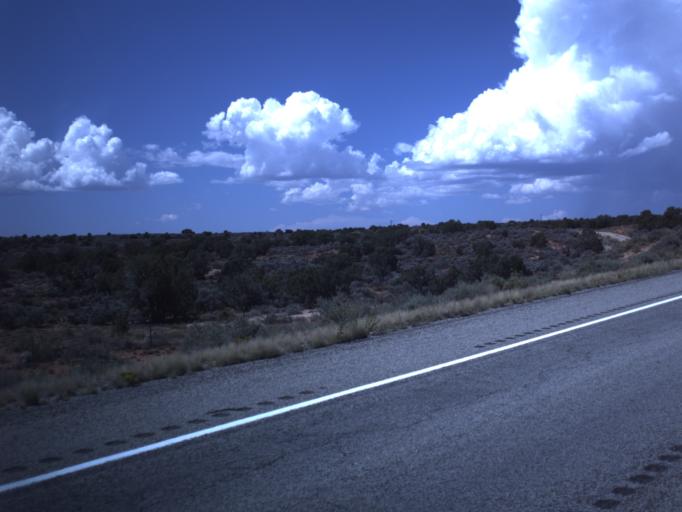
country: US
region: Utah
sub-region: San Juan County
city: Blanding
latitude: 37.4888
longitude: -109.4776
